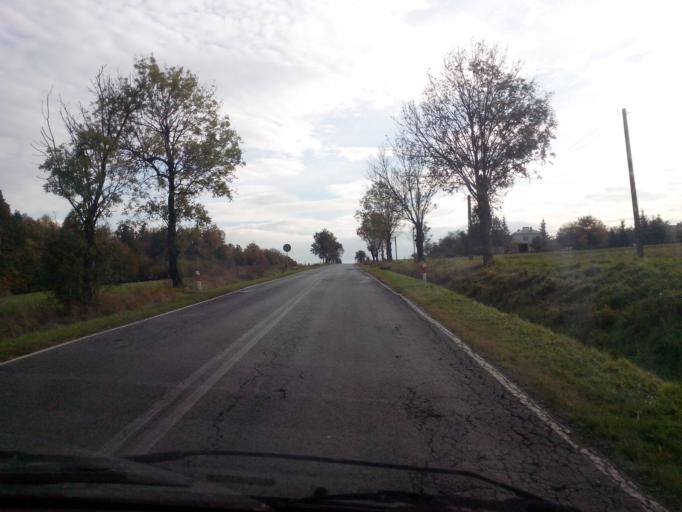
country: PL
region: Subcarpathian Voivodeship
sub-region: Powiat ropczycko-sedziszowski
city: Wielopole Skrzynskie
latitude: 49.9287
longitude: 21.6093
